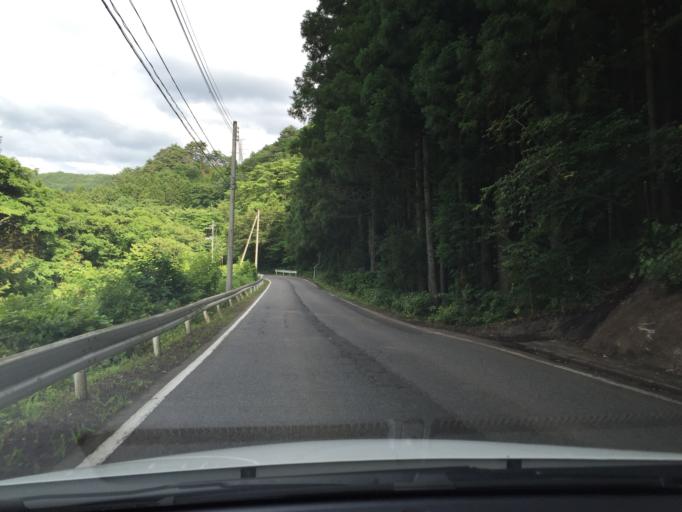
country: JP
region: Tochigi
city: Kuroiso
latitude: 37.2048
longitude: 140.1100
